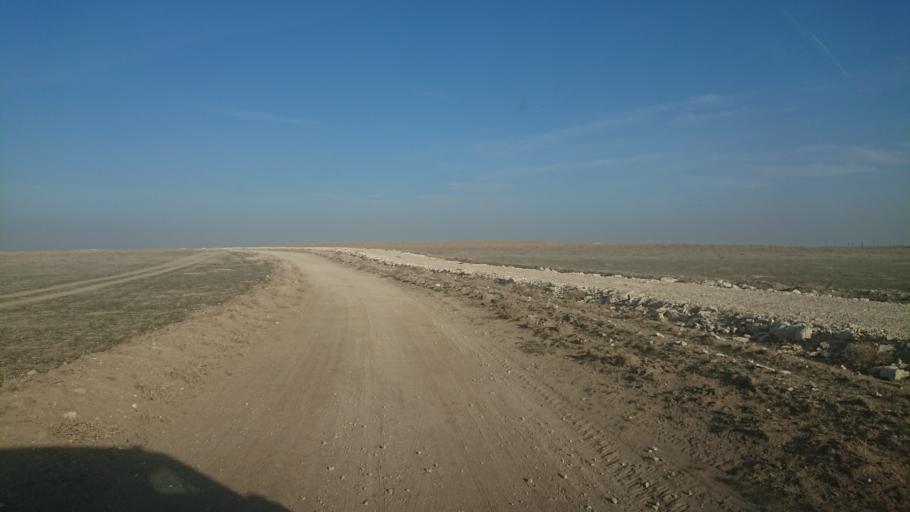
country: TR
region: Aksaray
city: Sultanhani
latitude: 38.1417
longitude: 33.5732
